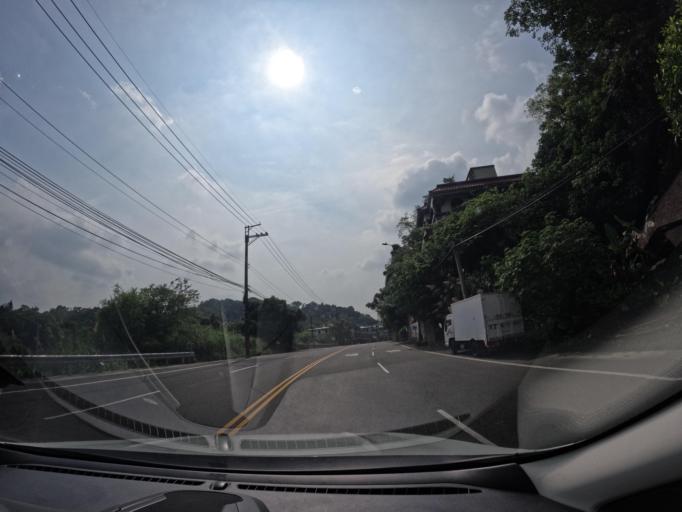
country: TW
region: Taiwan
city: Daxi
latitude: 24.8920
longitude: 121.3263
